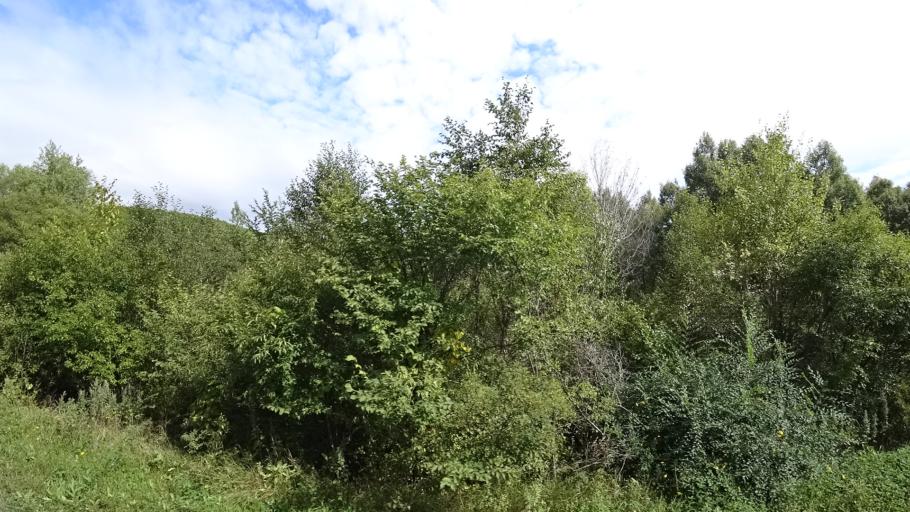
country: RU
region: Primorskiy
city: Lyalichi
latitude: 44.1482
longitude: 132.3902
